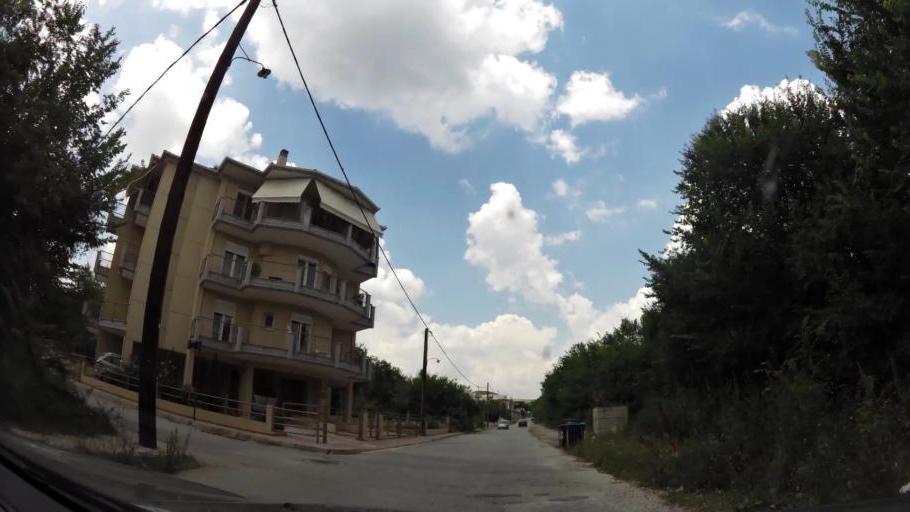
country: GR
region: West Macedonia
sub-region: Nomos Kozanis
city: Kozani
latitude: 40.3004
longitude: 21.8049
